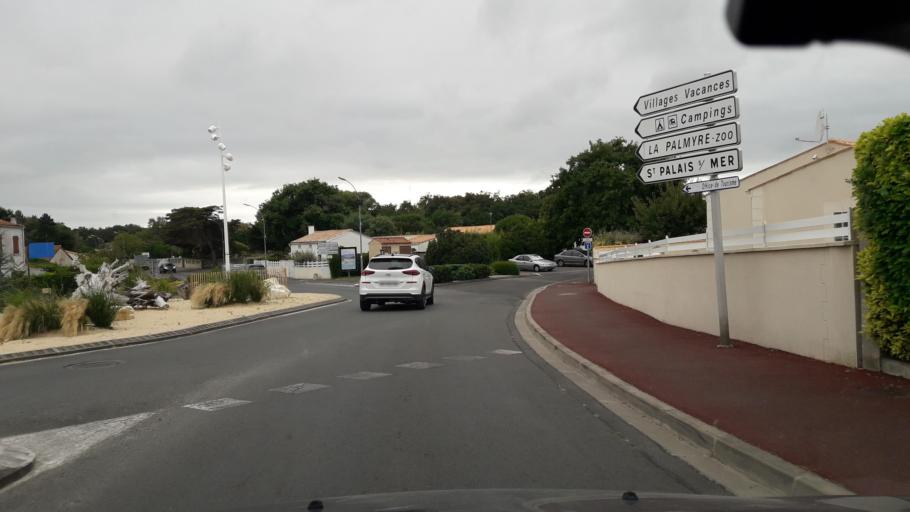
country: FR
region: Poitou-Charentes
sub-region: Departement de la Charente-Maritime
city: Les Mathes
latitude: 45.7166
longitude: -1.1509
